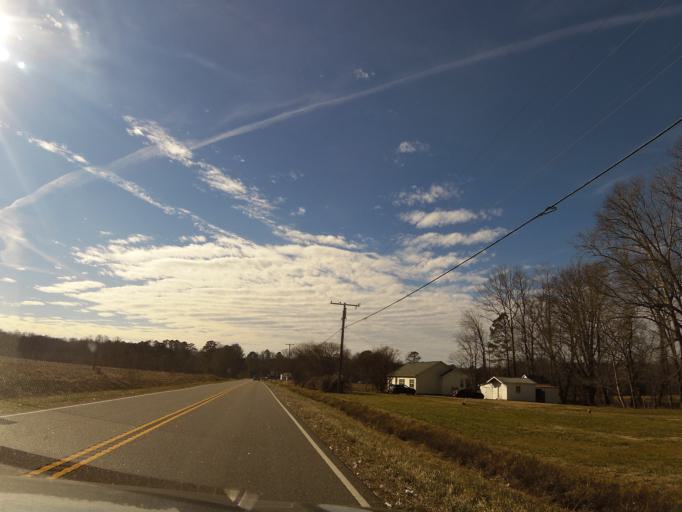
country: US
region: Virginia
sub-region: Isle of Wight County
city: Windsor
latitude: 36.7777
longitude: -76.8390
